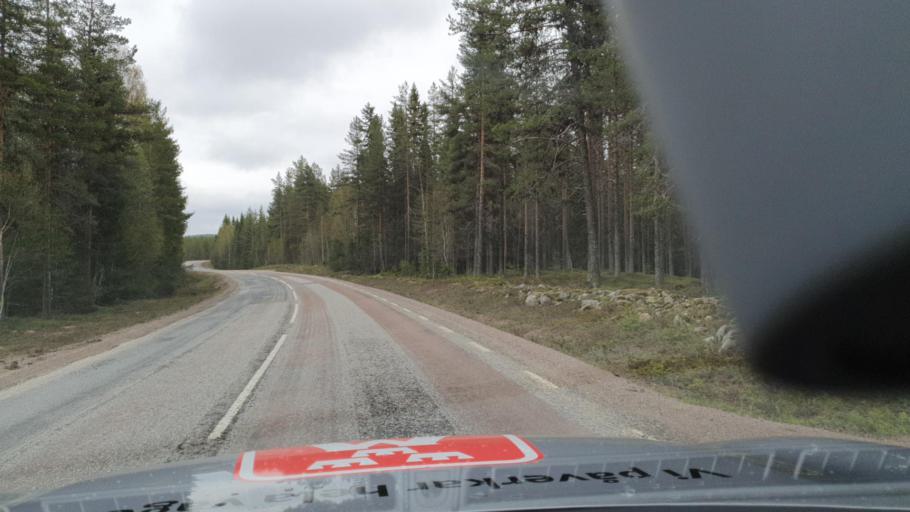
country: SE
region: Vaesternorrland
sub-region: Solleftea Kommun
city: Solleftea
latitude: 63.6612
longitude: 17.2645
